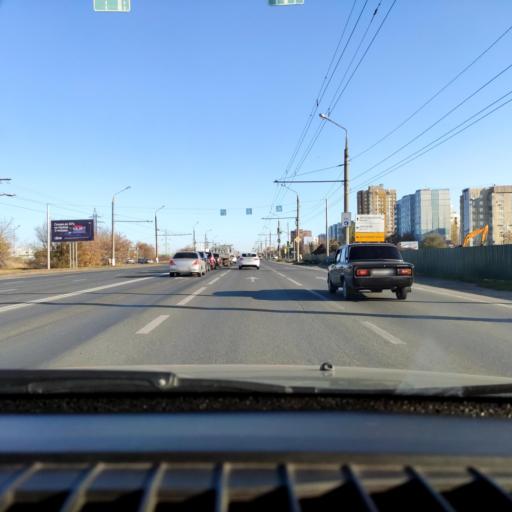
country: RU
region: Samara
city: Tol'yatti
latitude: 53.5496
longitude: 49.3300
